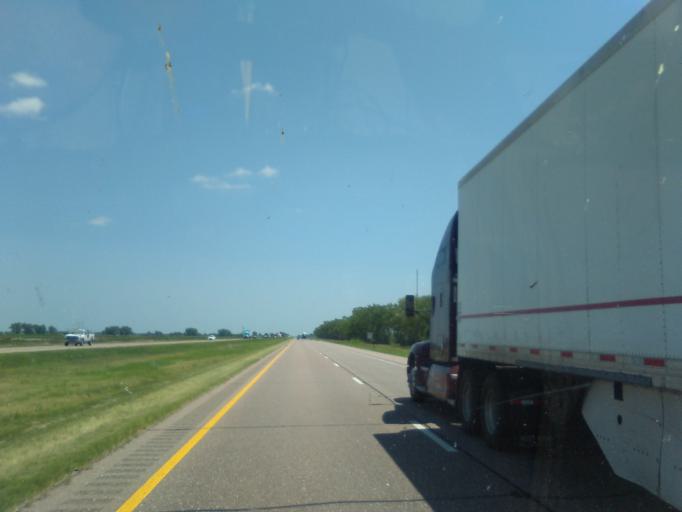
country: US
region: Nebraska
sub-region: Dawson County
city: Cozad
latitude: 40.8790
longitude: -100.0700
